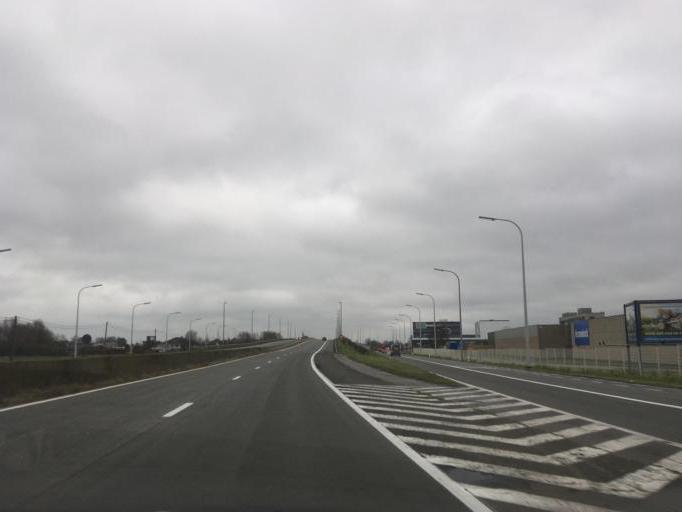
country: BE
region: Flanders
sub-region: Provincie West-Vlaanderen
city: Hooglede
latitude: 50.9788
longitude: 3.1131
